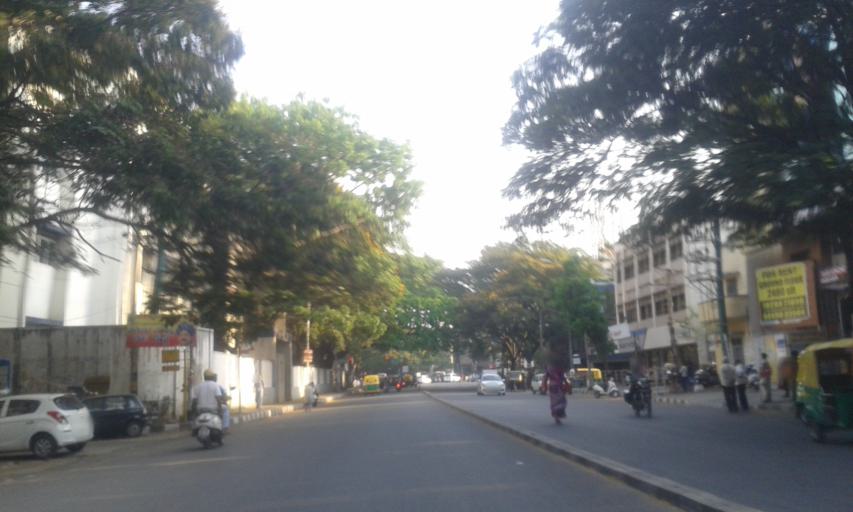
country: IN
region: Karnataka
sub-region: Bangalore Urban
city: Bangalore
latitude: 12.9498
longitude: 77.5801
